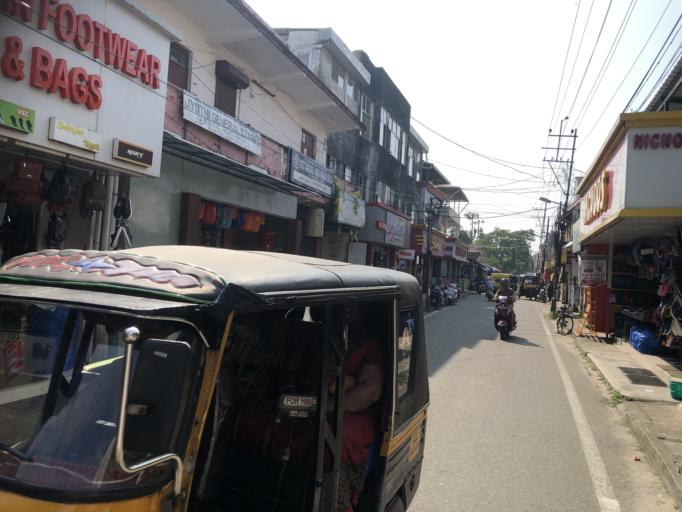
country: IN
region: Kerala
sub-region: Ernakulam
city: Cochin
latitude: 9.9578
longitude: 76.2542
